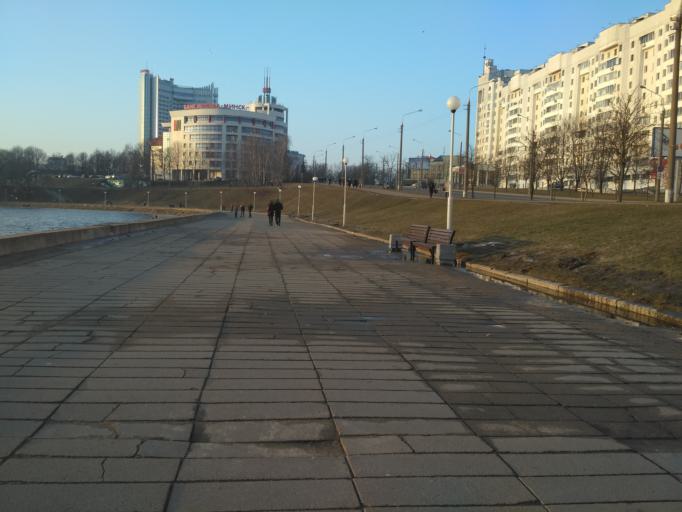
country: BY
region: Minsk
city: Minsk
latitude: 53.9121
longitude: 27.5550
